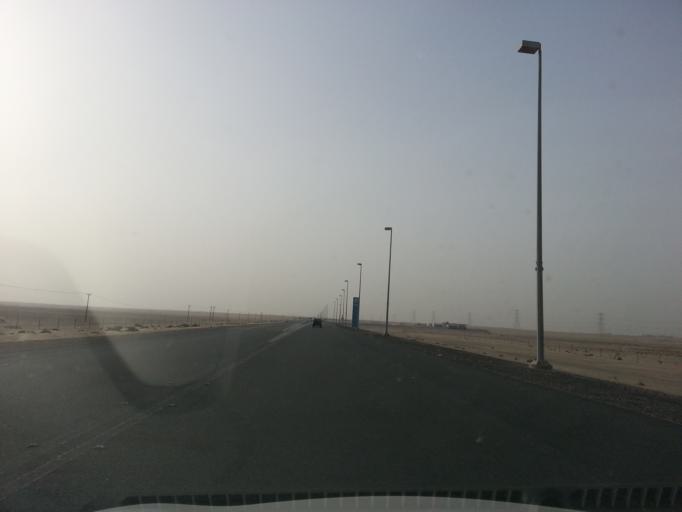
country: AE
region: Dubai
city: Dubai
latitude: 24.7985
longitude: 55.0728
